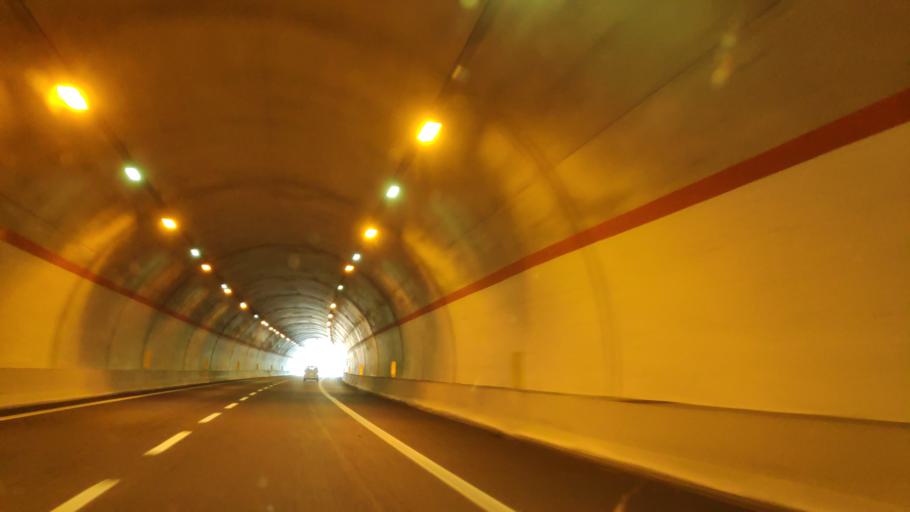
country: IT
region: Calabria
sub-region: Provincia di Cosenza
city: Morano Calabro
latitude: 39.8662
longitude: 16.0804
